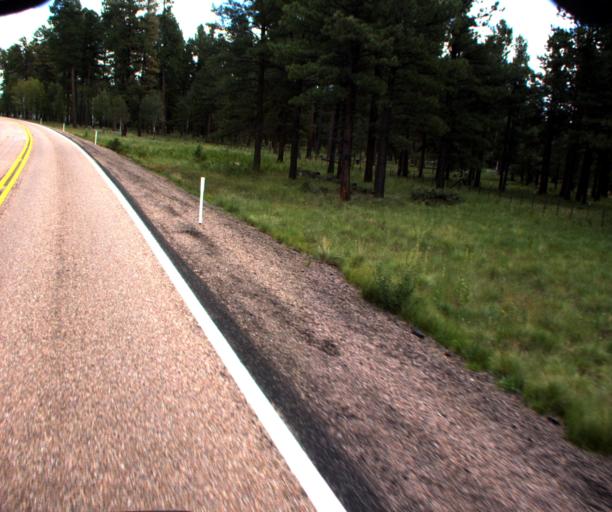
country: US
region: Arizona
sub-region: Navajo County
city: Pinetop-Lakeside
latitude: 34.0437
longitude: -109.7055
